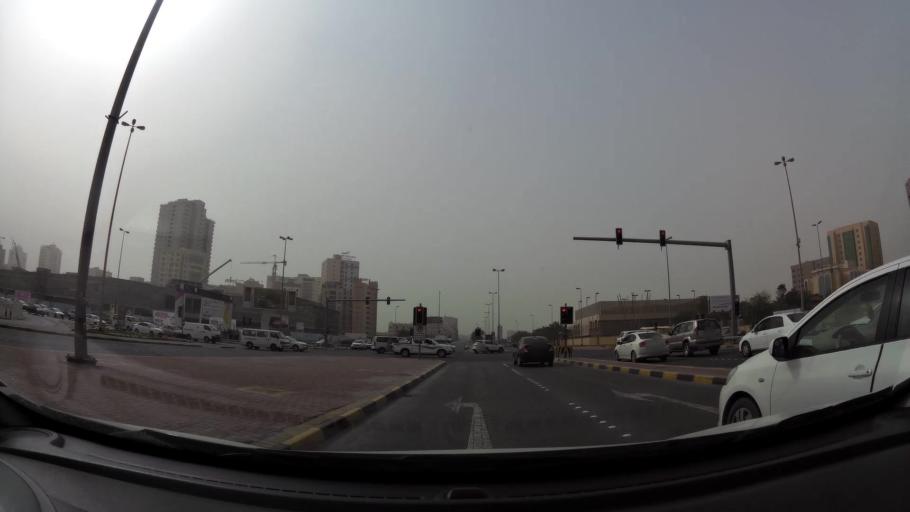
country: BH
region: Manama
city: Manama
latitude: 26.2172
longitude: 50.5970
